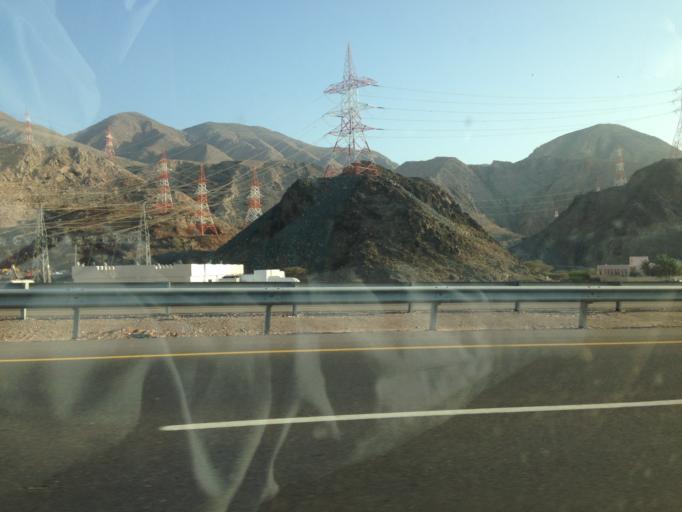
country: OM
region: Muhafazat Masqat
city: Bawshar
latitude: 23.5836
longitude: 58.4498
